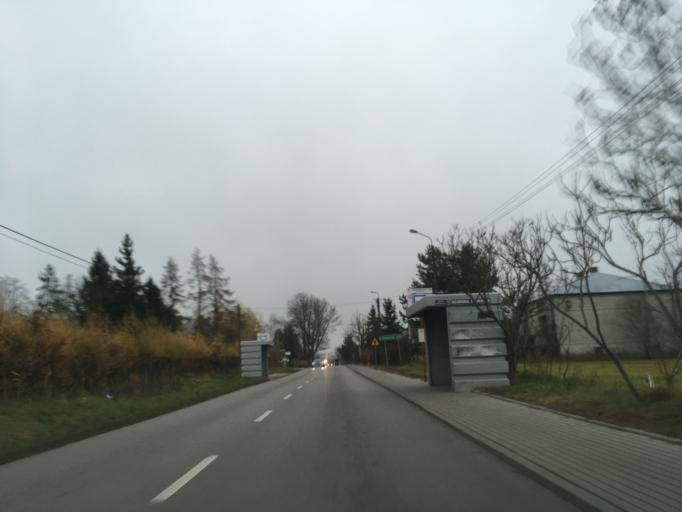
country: PL
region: Masovian Voivodeship
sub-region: Powiat piaseczynski
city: Lesznowola
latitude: 52.0551
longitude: 20.9243
